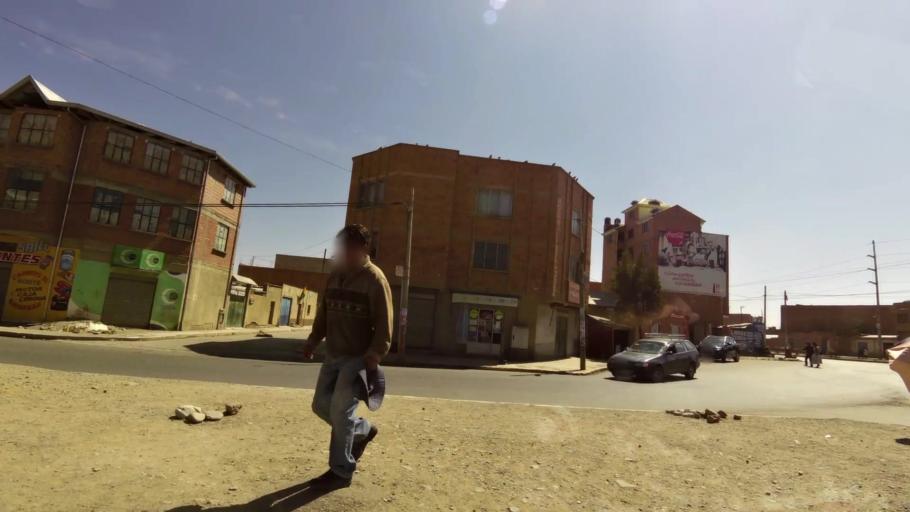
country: BO
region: La Paz
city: La Paz
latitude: -16.5420
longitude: -68.1689
